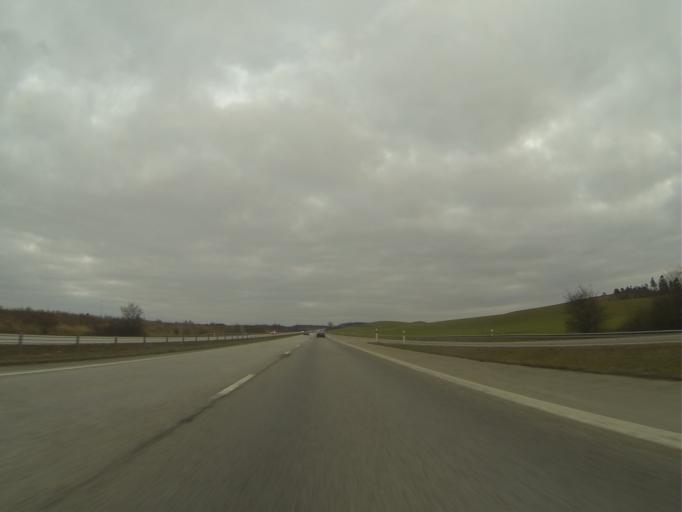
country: SE
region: Skane
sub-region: Malmo
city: Oxie
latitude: 55.5542
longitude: 13.1059
